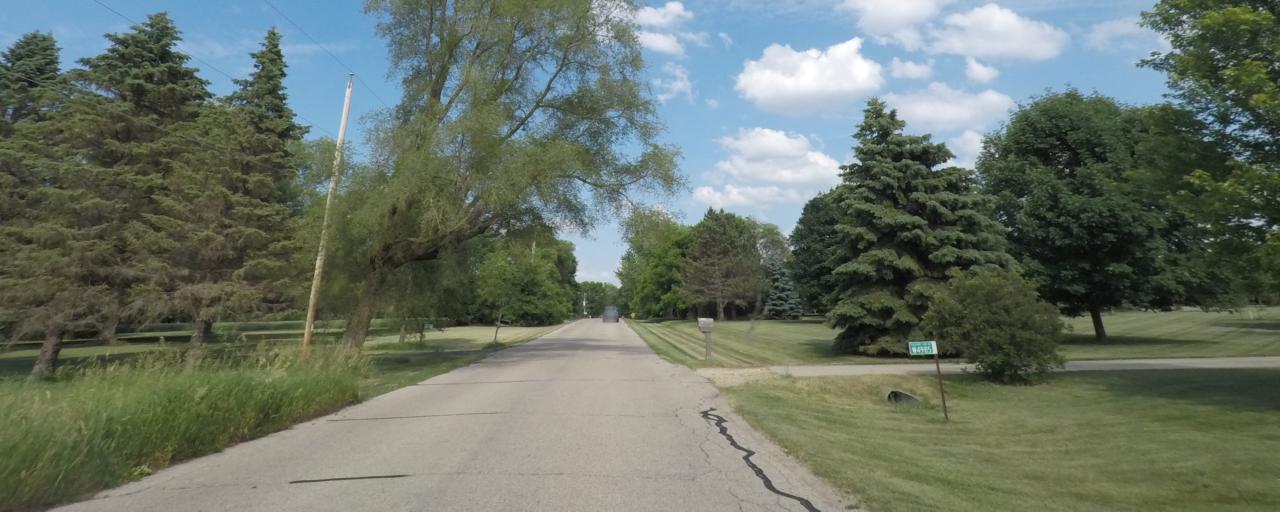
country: US
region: Wisconsin
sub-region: Walworth County
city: Elkhorn
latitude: 42.7640
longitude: -88.5483
